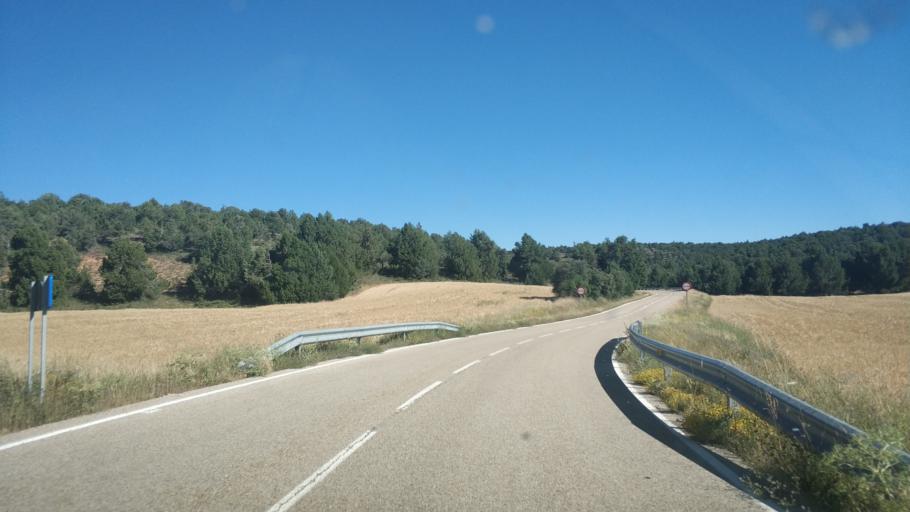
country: ES
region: Castille and Leon
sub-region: Provincia de Soria
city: Liceras
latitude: 41.4372
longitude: -3.2115
